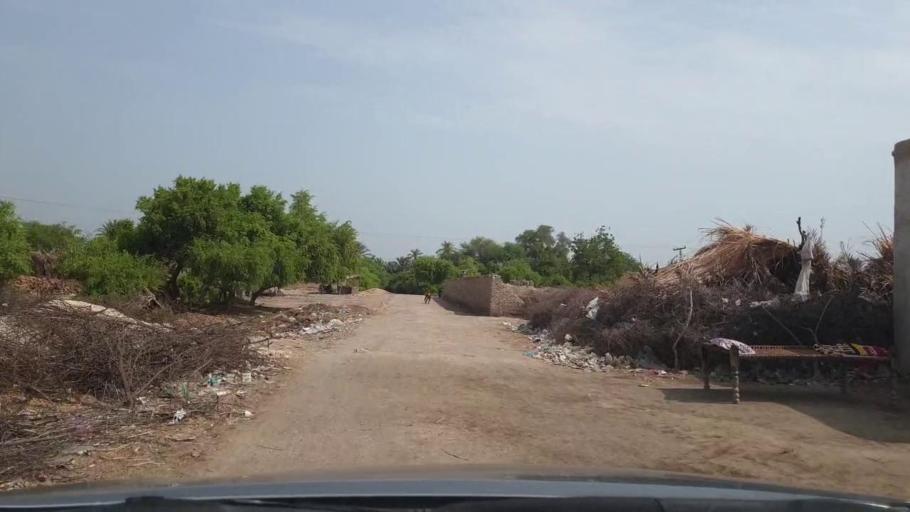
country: PK
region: Sindh
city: Rohri
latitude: 27.6462
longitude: 69.0235
